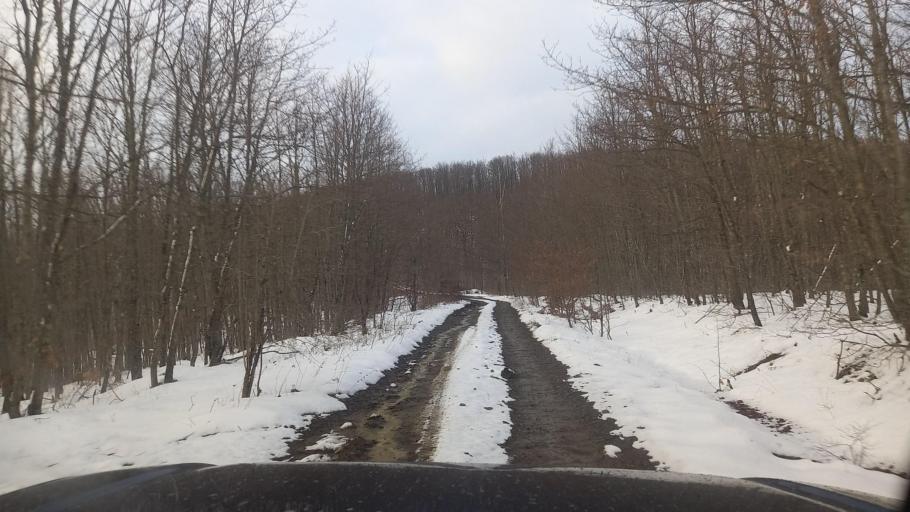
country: RU
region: Krasnodarskiy
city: Smolenskaya
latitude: 44.6807
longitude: 38.7671
